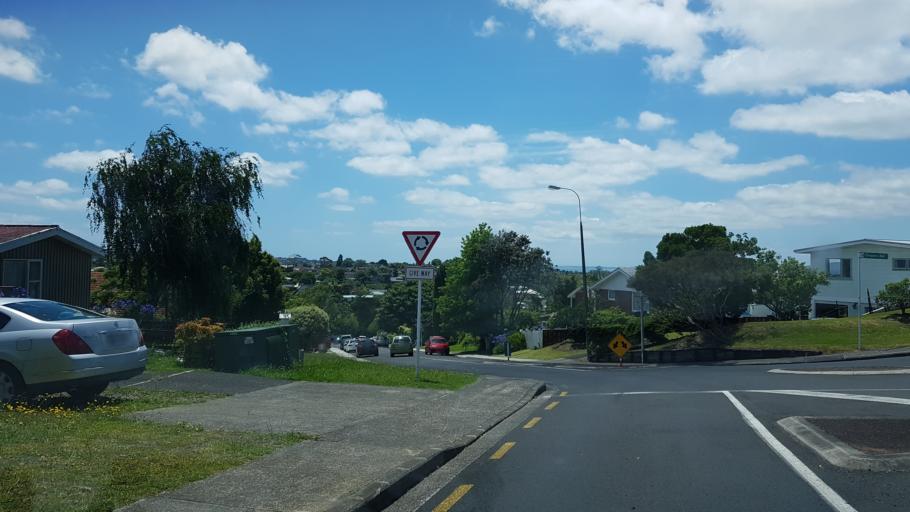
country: NZ
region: Auckland
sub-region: Auckland
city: North Shore
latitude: -36.7847
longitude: 174.7260
